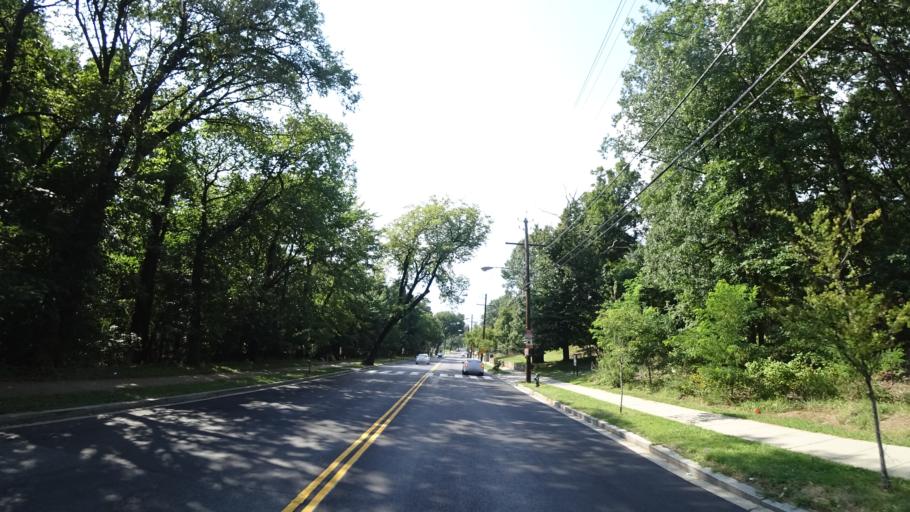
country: US
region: Maryland
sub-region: Prince George's County
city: Hillcrest Heights
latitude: 38.8632
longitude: -76.9732
